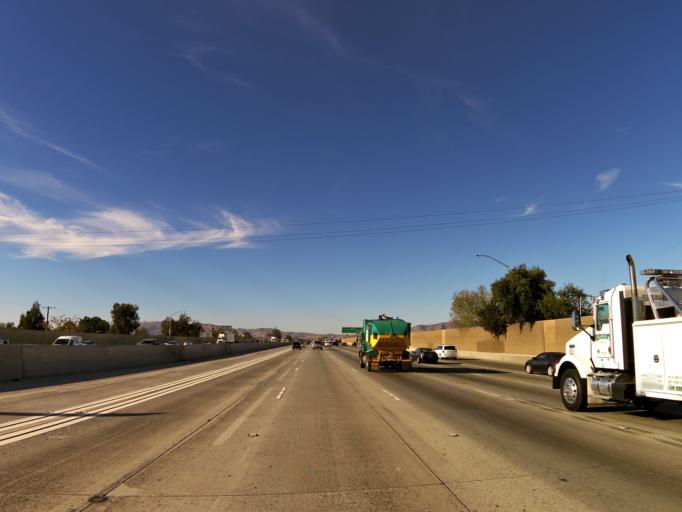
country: US
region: California
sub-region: Los Angeles County
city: San Fernando
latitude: 34.2475
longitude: -118.4250
